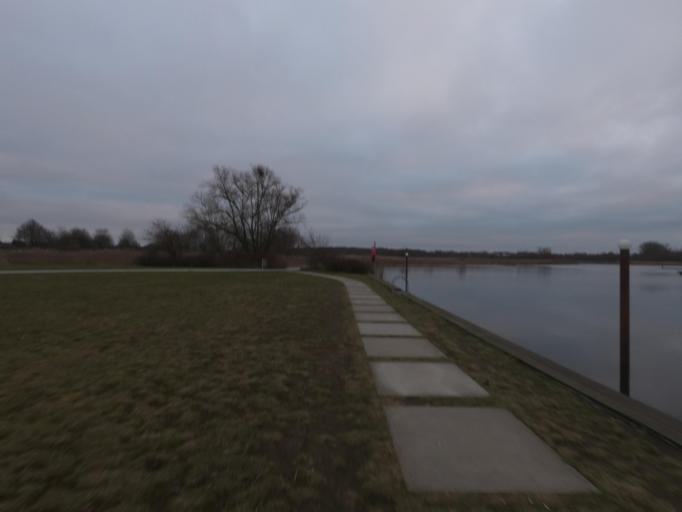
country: DE
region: Mecklenburg-Vorpommern
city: Rostock
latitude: 54.0903
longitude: 12.1528
